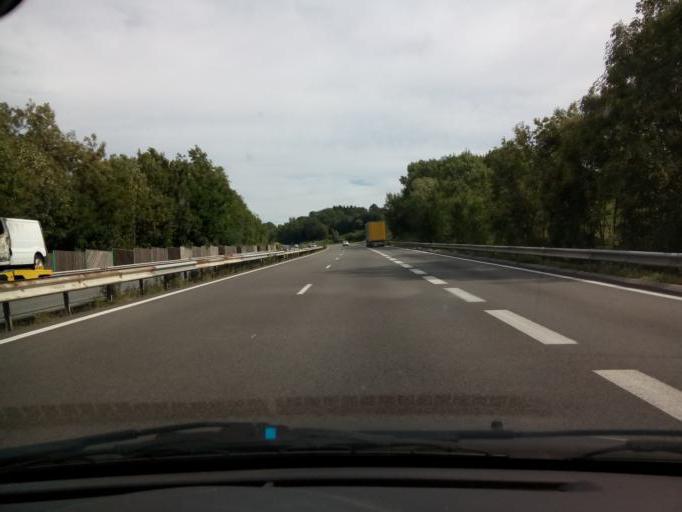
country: FR
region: Rhone-Alpes
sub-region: Departement de l'Isere
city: Saint-Victor-de-Cessieu
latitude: 45.5404
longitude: 5.3897
